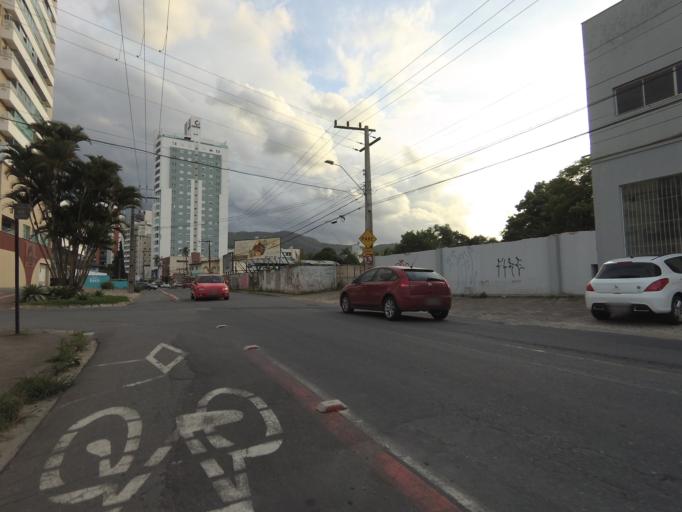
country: BR
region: Santa Catarina
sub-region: Blumenau
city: Blumenau
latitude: -26.9140
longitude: -49.0915
